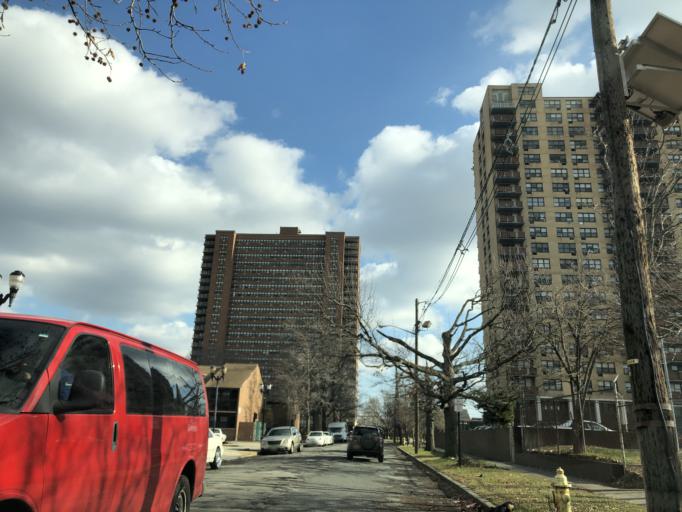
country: US
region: New Jersey
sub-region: Camden County
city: Camden
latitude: 39.9496
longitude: -75.1179
